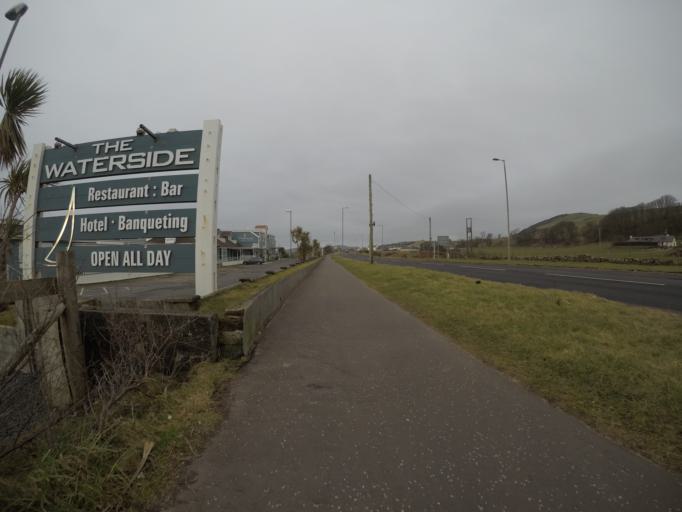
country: GB
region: Scotland
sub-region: North Ayrshire
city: West Kilbride
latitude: 55.6745
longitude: -4.8515
